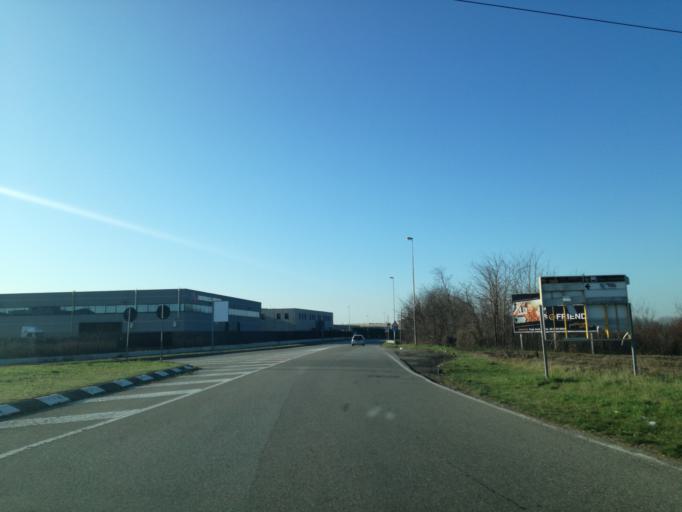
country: IT
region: Lombardy
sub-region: Provincia di Monza e Brianza
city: Villanova
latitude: 45.6365
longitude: 9.3971
